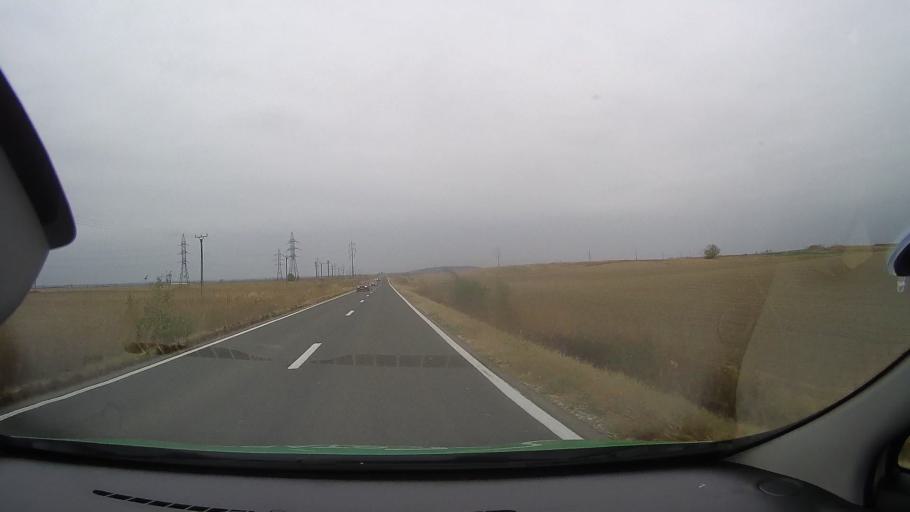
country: RO
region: Constanta
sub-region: Comuna Ciobanu
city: Ciobanu
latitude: 44.6976
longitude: 27.9969
